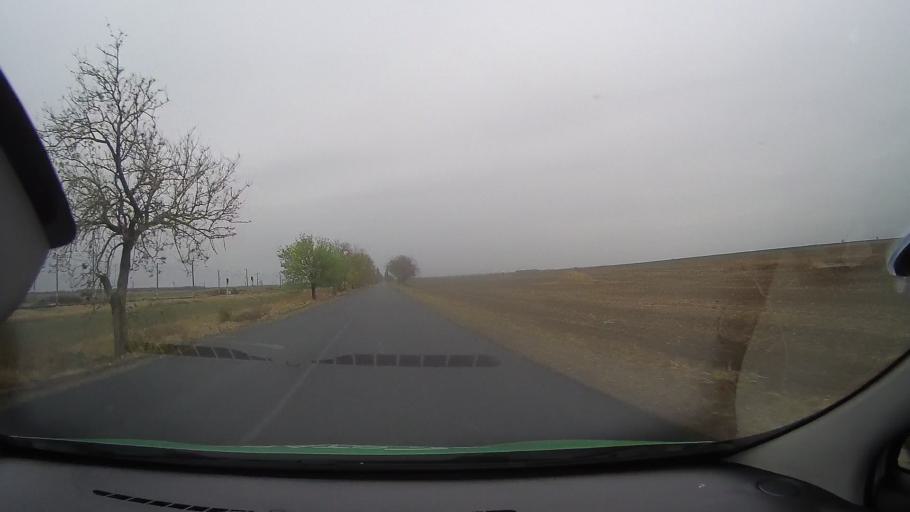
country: RO
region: Ialomita
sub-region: Comuna Valea Ciorii
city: Valea Ciorii
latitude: 44.7022
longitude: 27.5967
